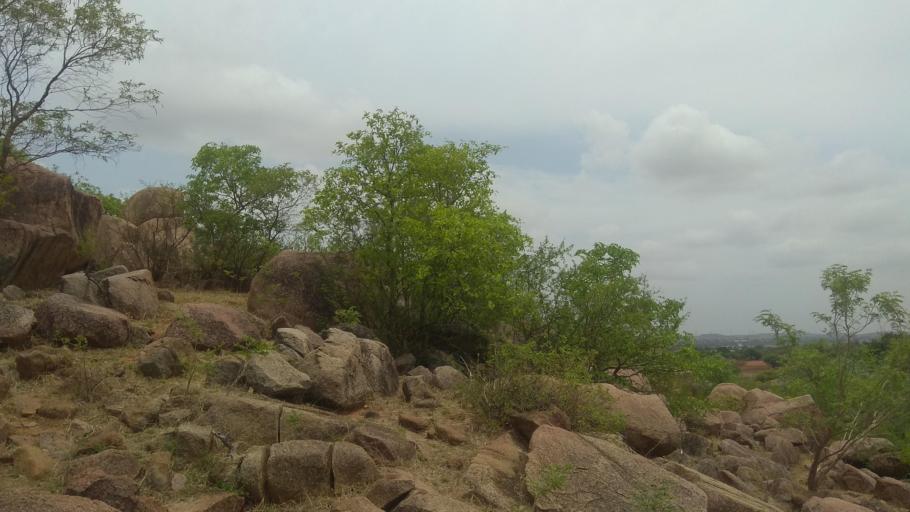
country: IN
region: Telangana
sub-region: Mahbubnagar
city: Farrukhnagar
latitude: 16.8930
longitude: 78.4892
